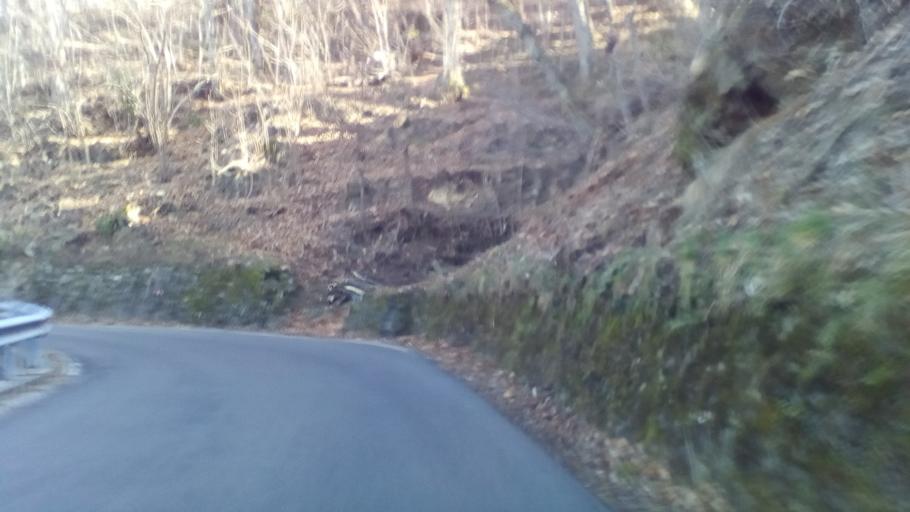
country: IT
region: Tuscany
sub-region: Provincia di Lucca
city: Castiglione di Garfagnana
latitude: 44.1444
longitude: 10.4346
